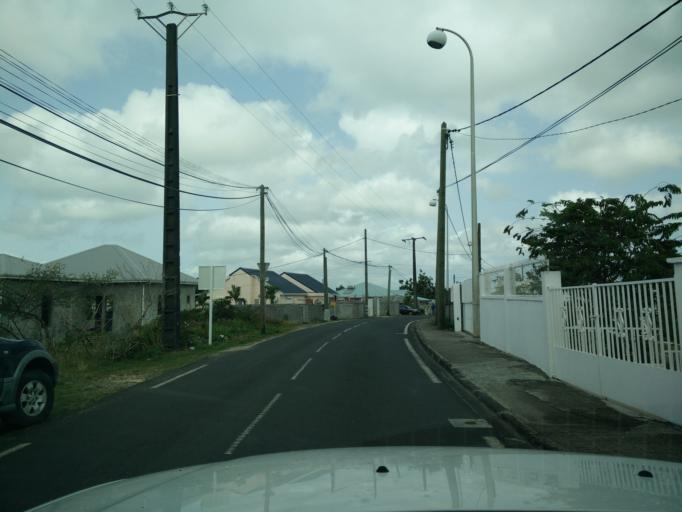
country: GP
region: Guadeloupe
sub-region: Guadeloupe
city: Le Gosier
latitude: 16.2182
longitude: -61.4561
